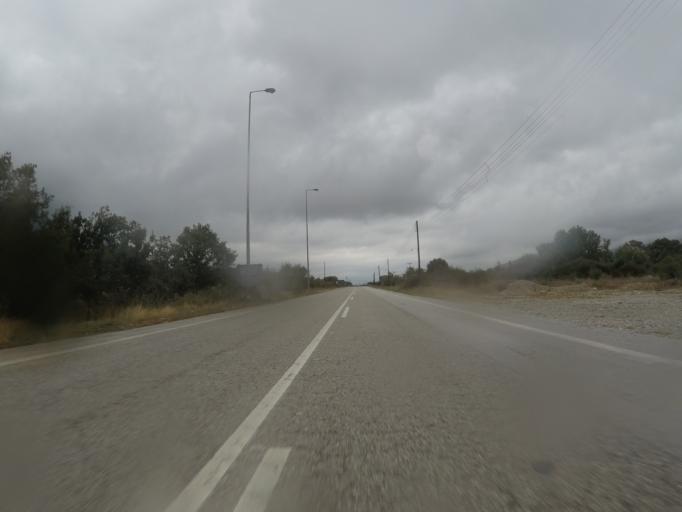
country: GR
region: Peloponnese
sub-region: Nomos Arkadias
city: Tripoli
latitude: 37.5931
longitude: 22.4291
